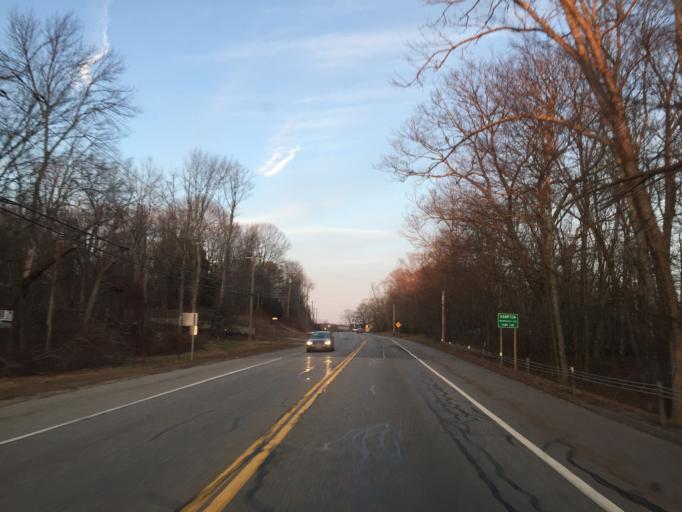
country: US
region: Connecticut
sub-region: Windham County
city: Windham
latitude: 41.7681
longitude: -72.0975
